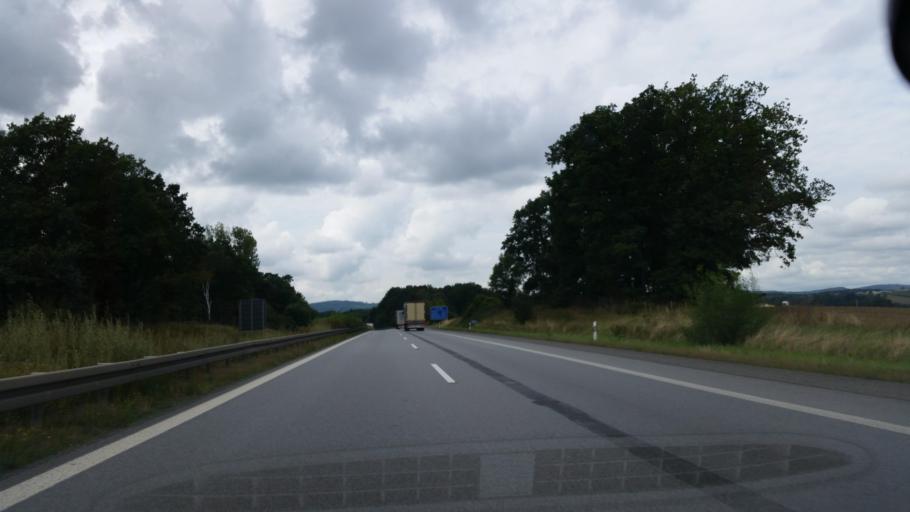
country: DE
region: Saxony
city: Burkau
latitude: 51.1978
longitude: 14.2146
